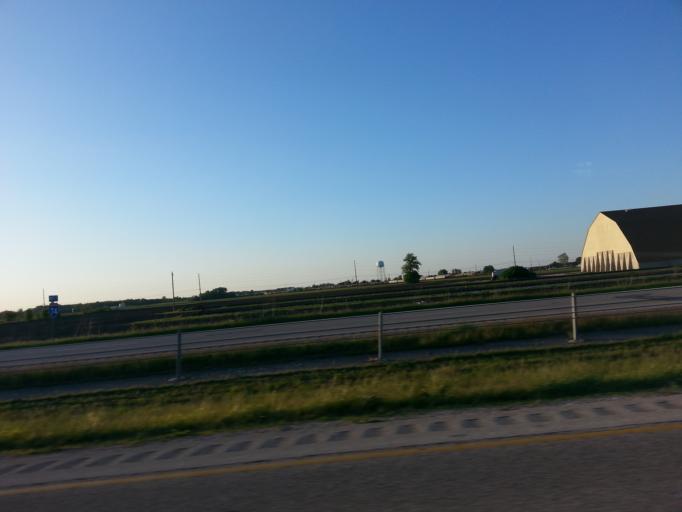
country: US
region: Illinois
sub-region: Vermilion County
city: Danville
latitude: 40.1155
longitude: -87.5528
